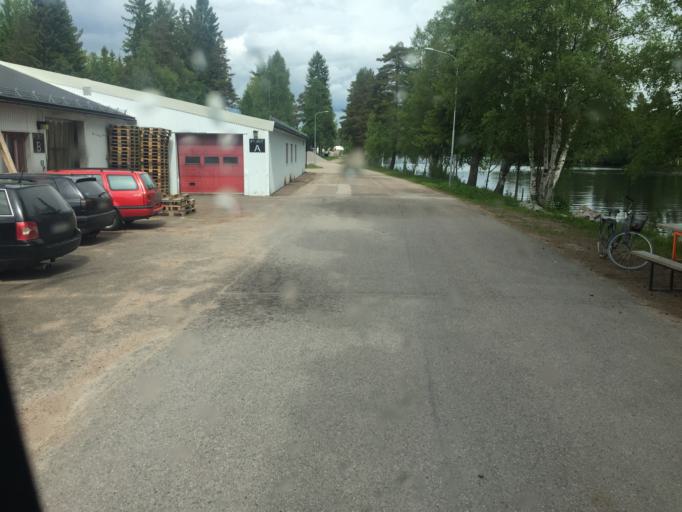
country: SE
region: Dalarna
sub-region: Vansbro Kommun
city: Vansbro
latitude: 60.5014
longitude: 14.2273
